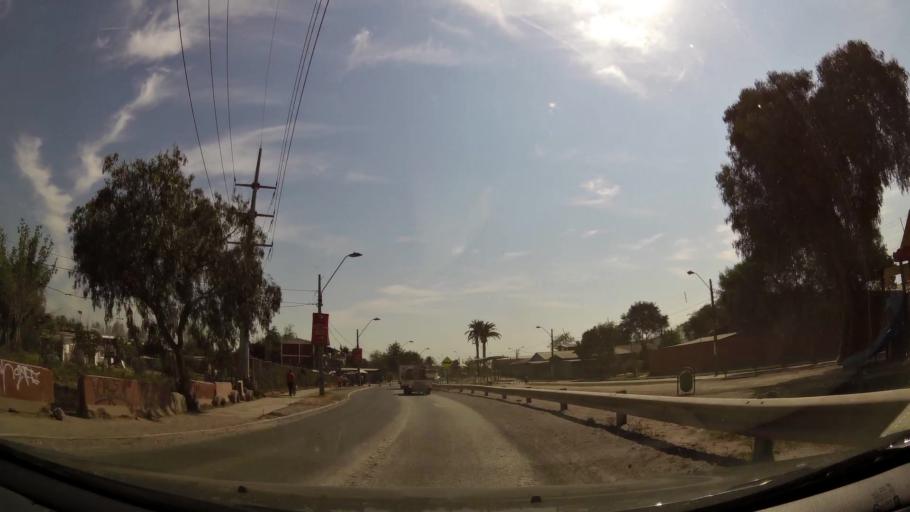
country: CL
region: Santiago Metropolitan
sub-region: Provincia de Santiago
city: La Pintana
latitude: -33.5672
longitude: -70.5981
